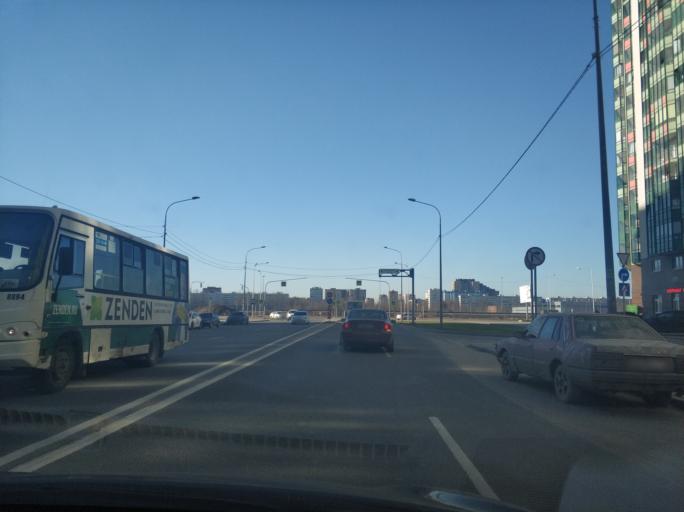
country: RU
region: St.-Petersburg
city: Grazhdanka
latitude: 60.0509
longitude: 30.4236
